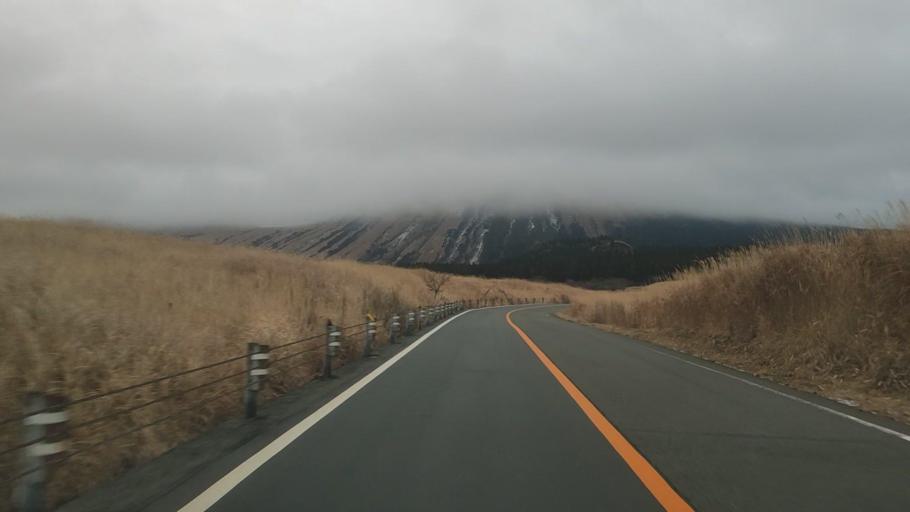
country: JP
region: Kumamoto
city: Aso
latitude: 32.9030
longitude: 131.0397
